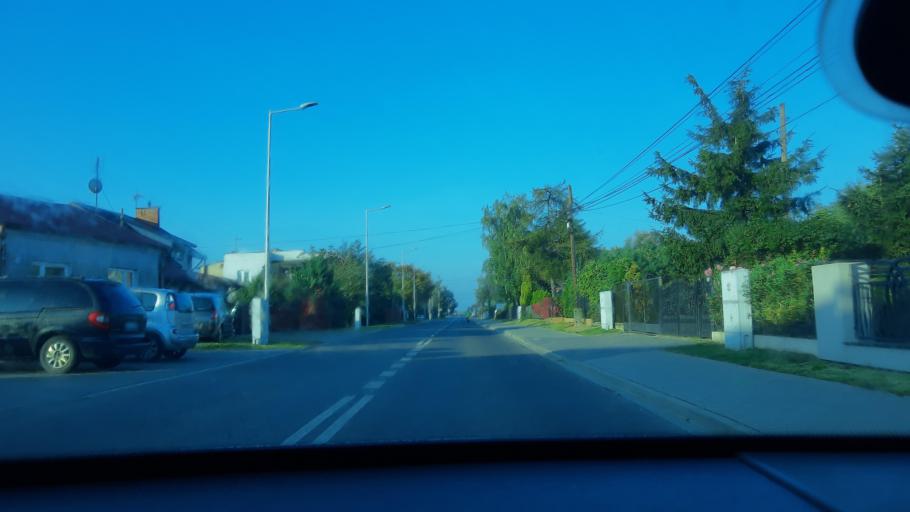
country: PL
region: Lodz Voivodeship
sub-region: Powiat sieradzki
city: Sieradz
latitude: 51.5943
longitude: 18.7121
